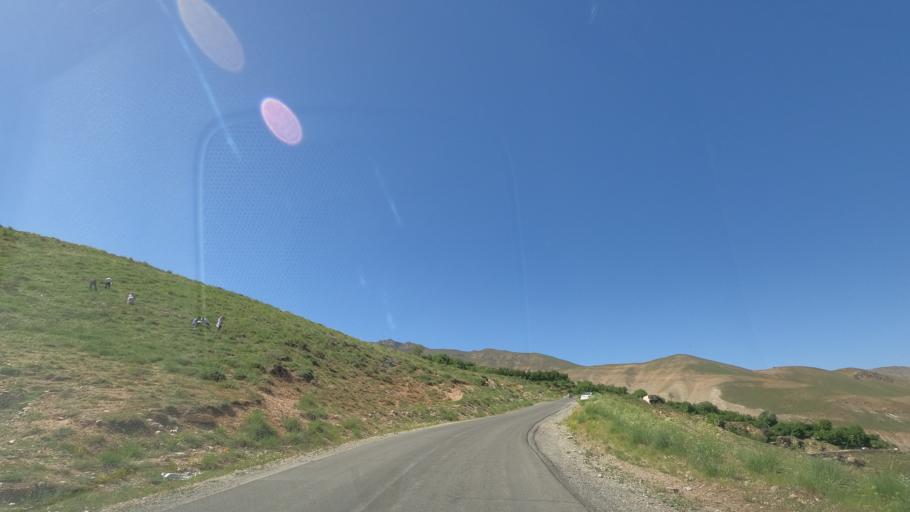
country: IR
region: Alborz
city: Karaj
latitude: 35.9245
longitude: 51.1577
